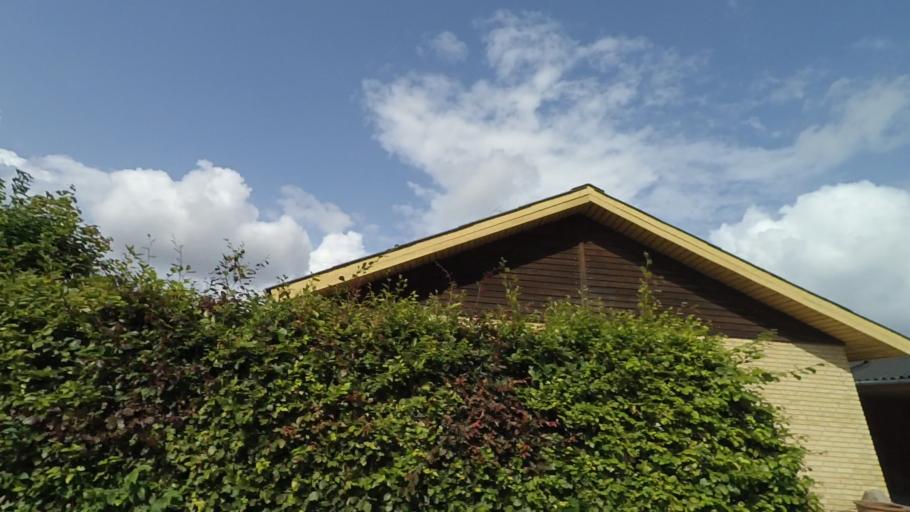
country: DK
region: Central Jutland
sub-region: Norddjurs Kommune
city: Allingabro
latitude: 56.4995
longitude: 10.3382
